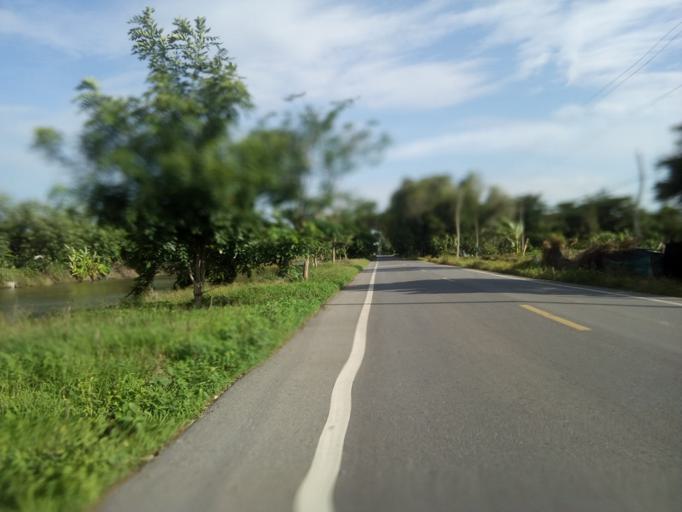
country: TH
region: Pathum Thani
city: Nong Suea
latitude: 14.1173
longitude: 100.8460
